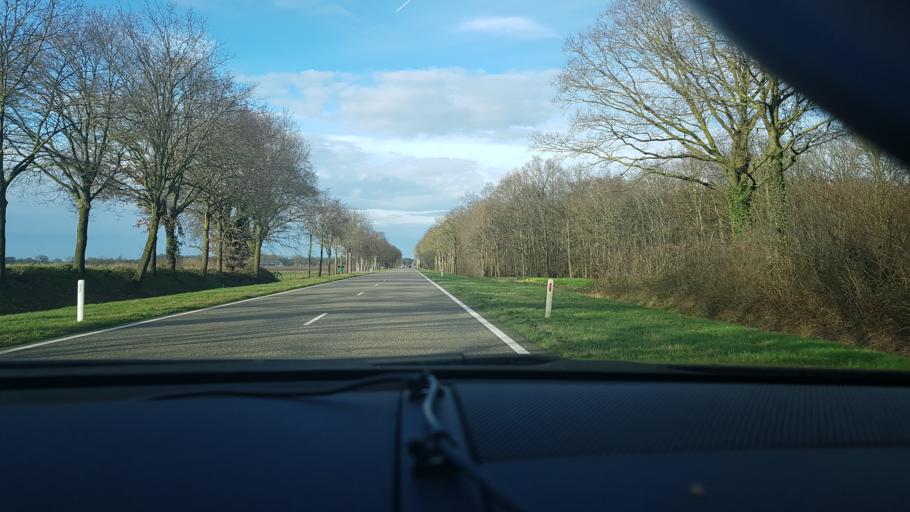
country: NL
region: Limburg
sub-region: Gemeente Peel en Maas
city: Maasbree
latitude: 51.3408
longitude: 6.0283
